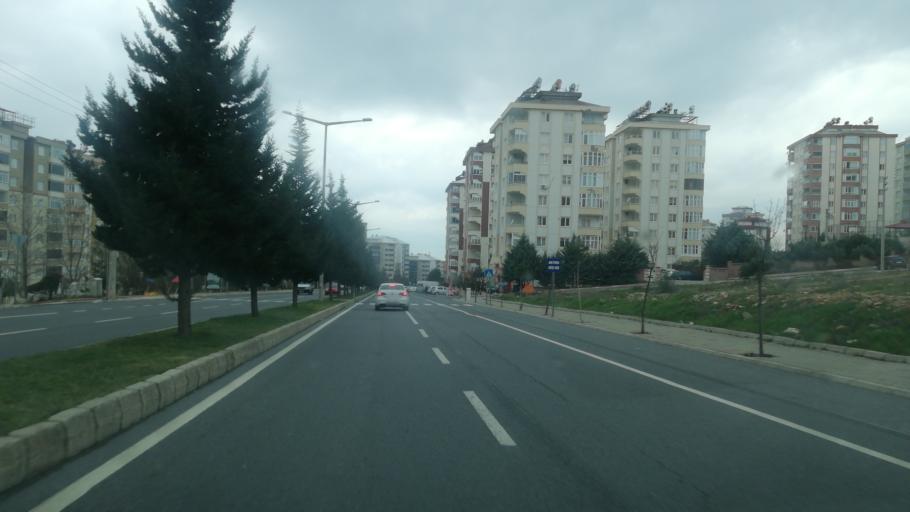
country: TR
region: Kahramanmaras
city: Kahramanmaras
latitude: 37.5912
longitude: 36.8811
